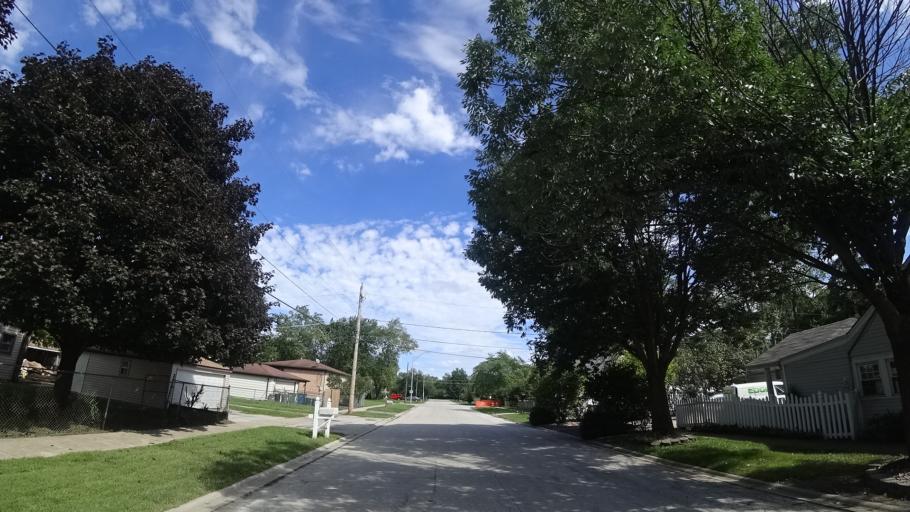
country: US
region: Illinois
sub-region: Cook County
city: Chicago Ridge
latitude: 41.7106
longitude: -87.7743
